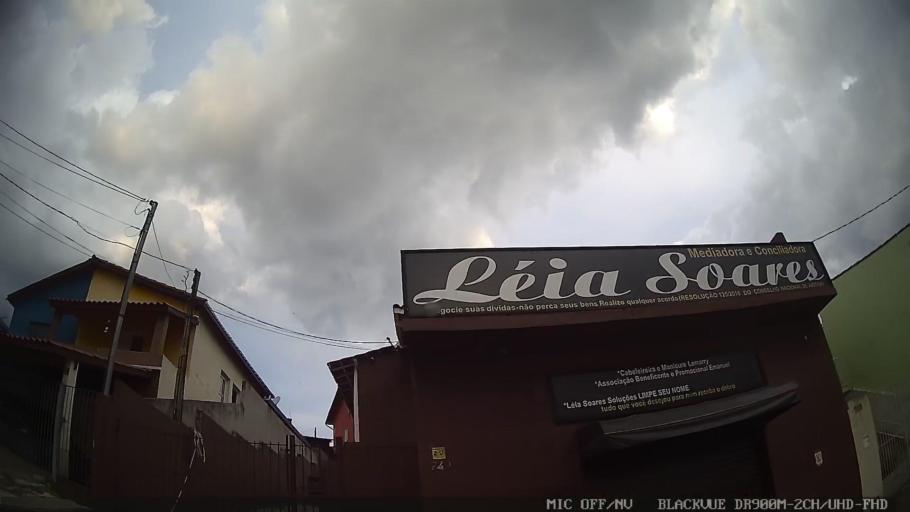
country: BR
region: Sao Paulo
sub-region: Braganca Paulista
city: Braganca Paulista
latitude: -22.9213
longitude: -46.5293
